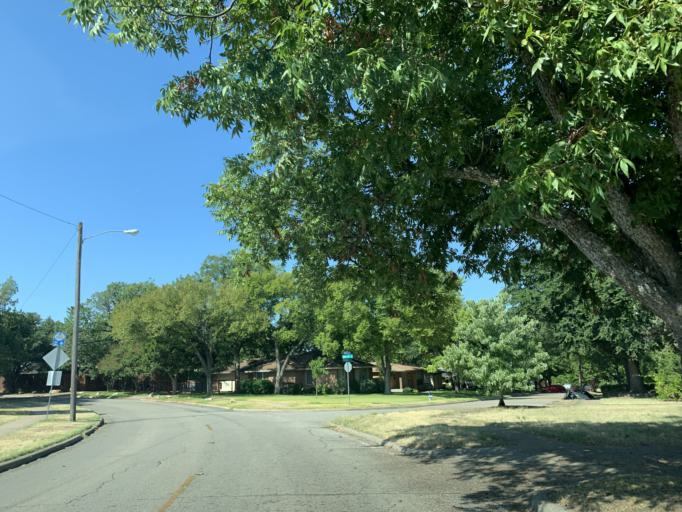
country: US
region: Texas
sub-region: Dallas County
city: Cockrell Hill
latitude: 32.7442
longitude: -96.8631
